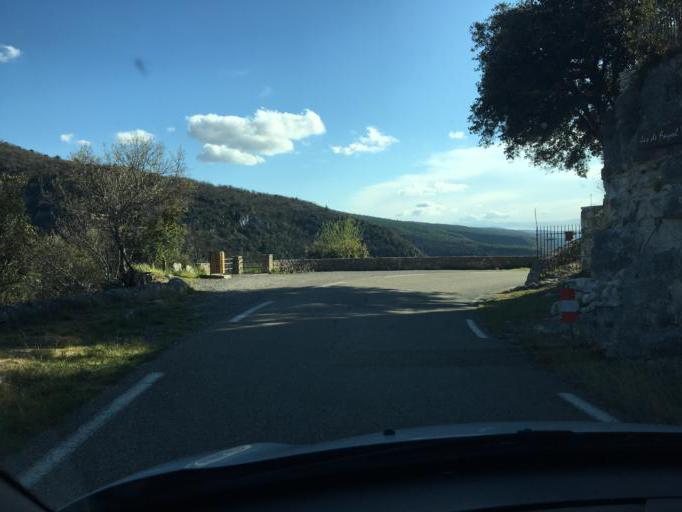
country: FR
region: Provence-Alpes-Cote d'Azur
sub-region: Departement du Vaucluse
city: Villes-sur-Auzon
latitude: 44.0554
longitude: 5.2945
